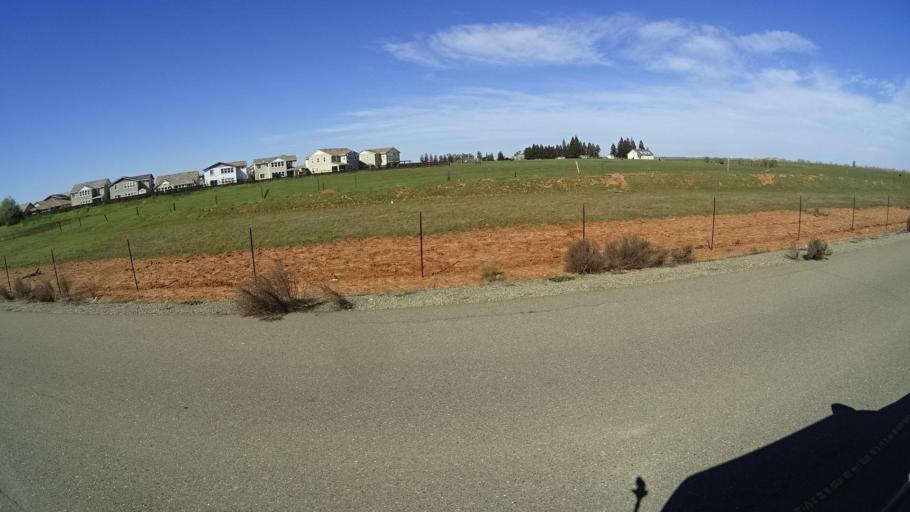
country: US
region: California
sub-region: Sacramento County
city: Gold River
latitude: 38.5726
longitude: -121.1929
